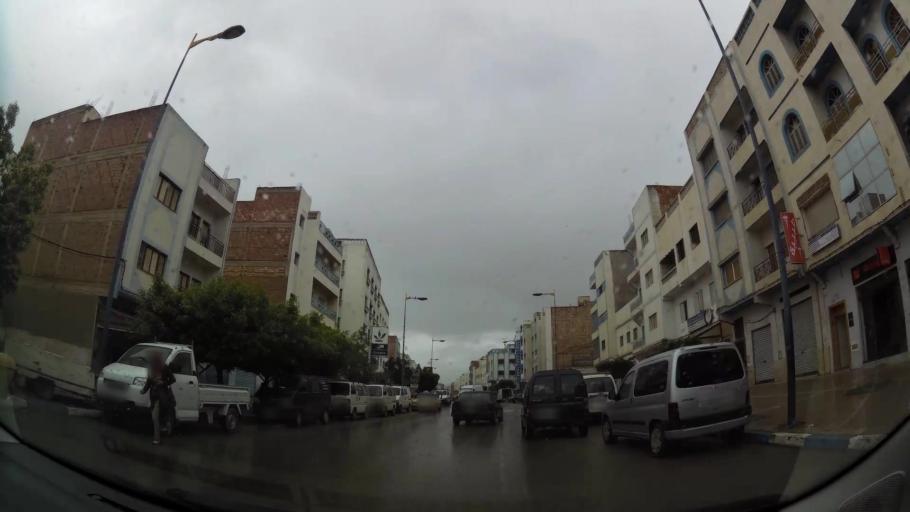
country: MA
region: Taza-Al Hoceima-Taounate
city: Imzourene
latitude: 35.1447
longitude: -3.8515
